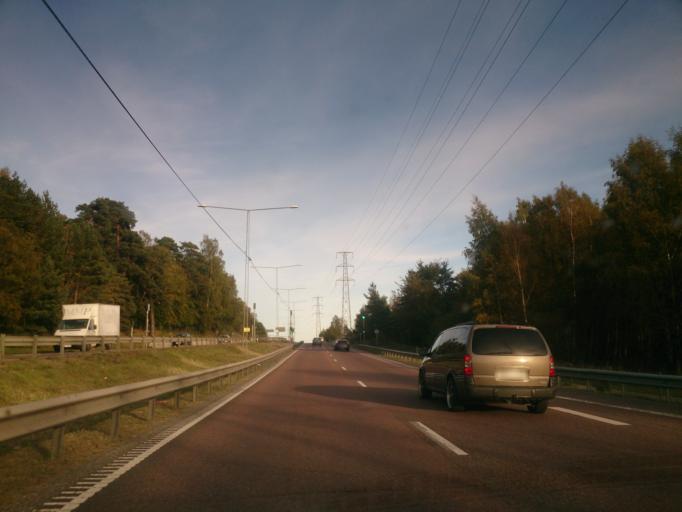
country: SE
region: Stockholm
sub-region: Stockholms Kommun
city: Arsta
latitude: 59.2612
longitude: 18.1052
